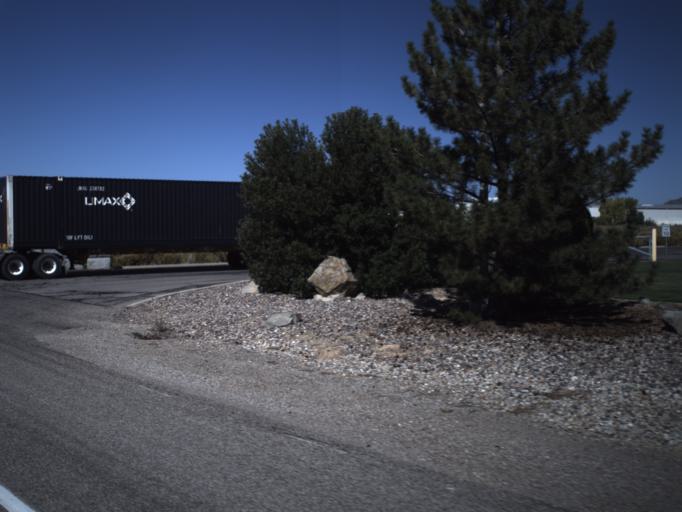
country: US
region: Utah
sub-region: Iron County
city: Cedar City
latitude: 37.6850
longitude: -113.1503
